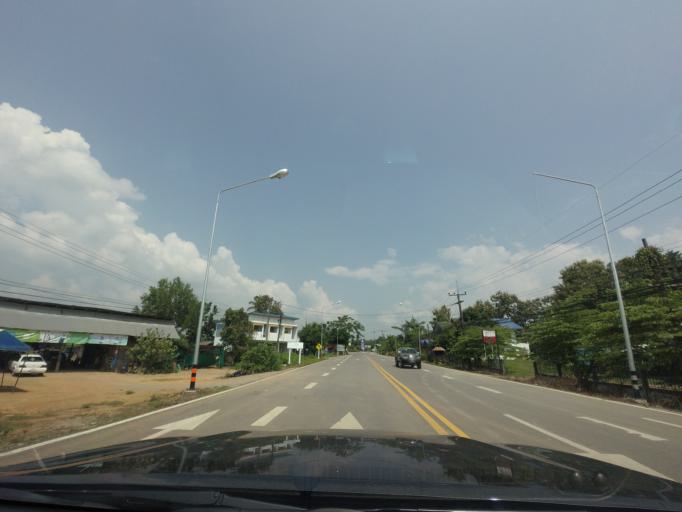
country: TH
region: Nan
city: Santi Suk
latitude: 18.9268
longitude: 100.9312
